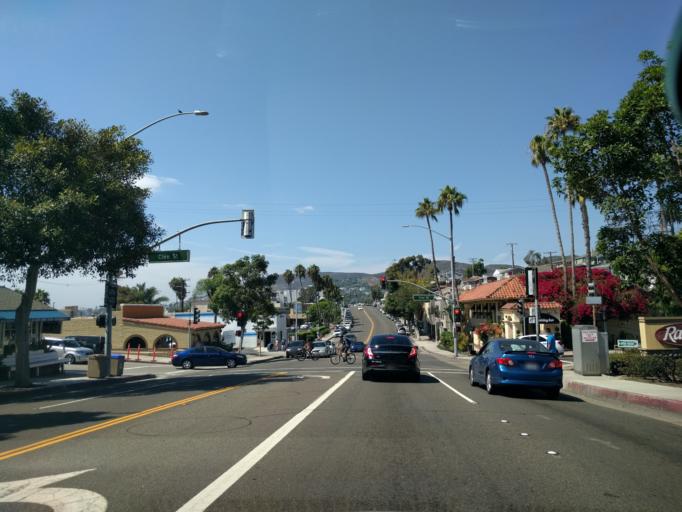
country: US
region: California
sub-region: Orange County
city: Laguna Beach
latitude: 33.5374
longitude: -117.7794
